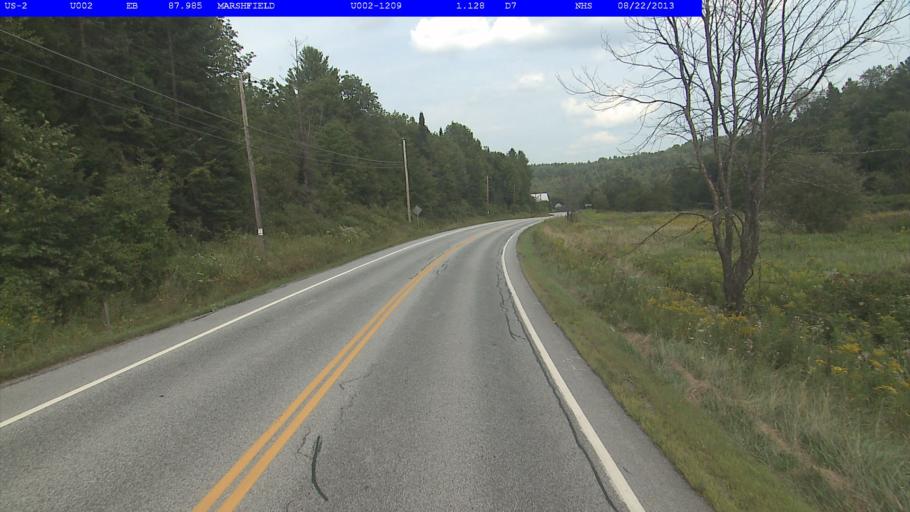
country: US
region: Vermont
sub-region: Washington County
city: Barre
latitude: 44.2898
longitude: -72.4047
